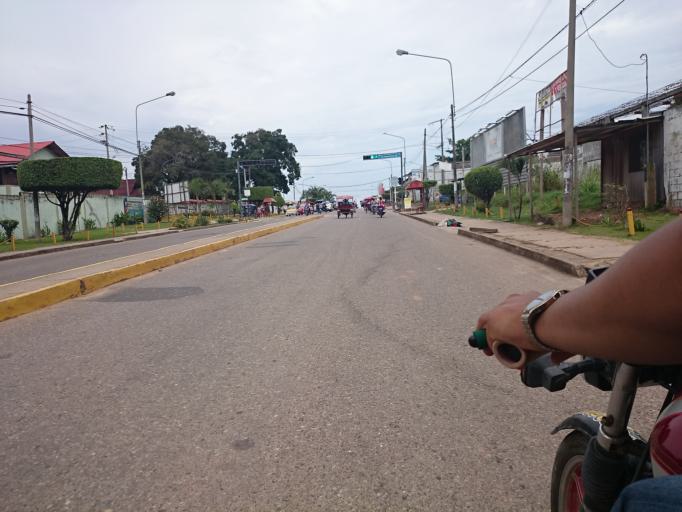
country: PE
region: Ucayali
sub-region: Provincia de Coronel Portillo
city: Puerto Callao
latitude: -8.3610
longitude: -74.5700
